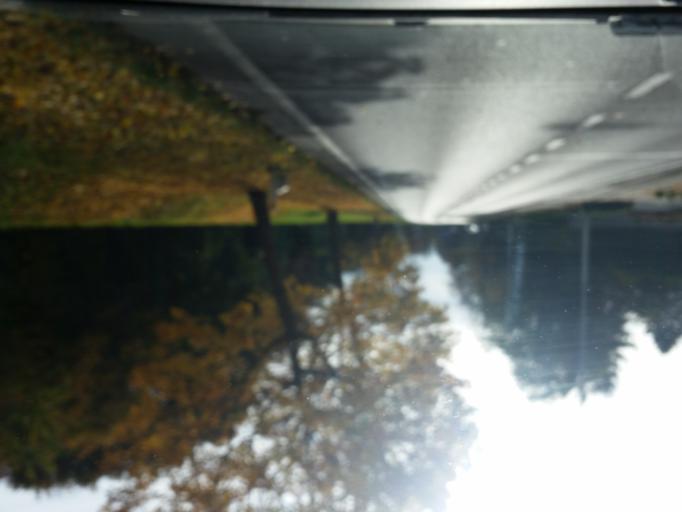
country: BE
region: Flanders
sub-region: Provincie Vlaams-Brabant
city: Grimbergen
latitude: 50.9234
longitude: 4.3651
